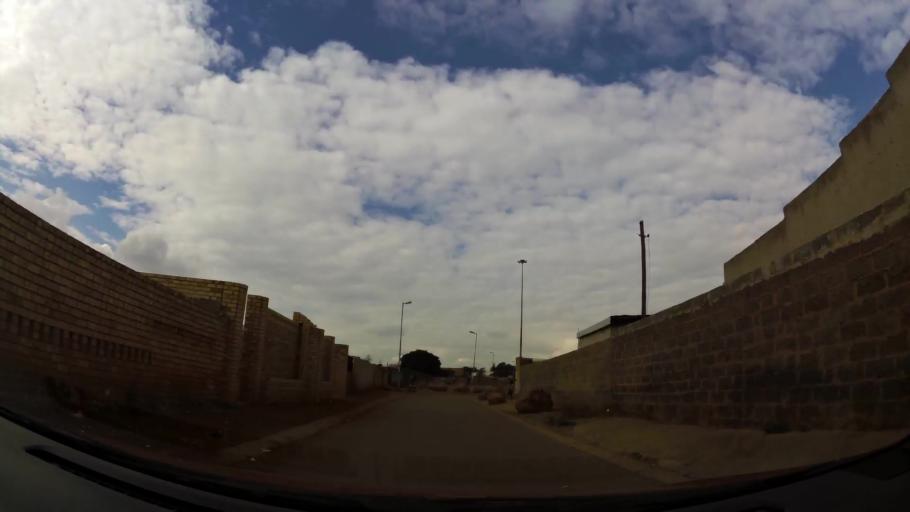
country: ZA
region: Gauteng
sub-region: City of Johannesburg Metropolitan Municipality
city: Soweto
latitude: -26.2453
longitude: 27.8523
